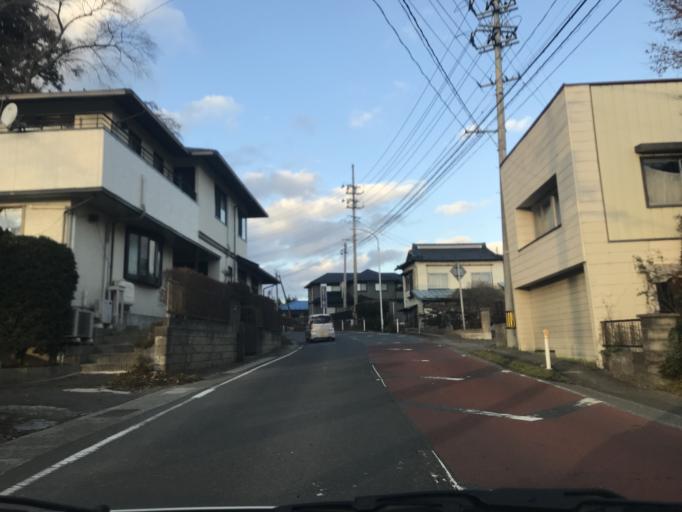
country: JP
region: Miyagi
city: Furukawa
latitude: 38.6615
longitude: 141.0111
